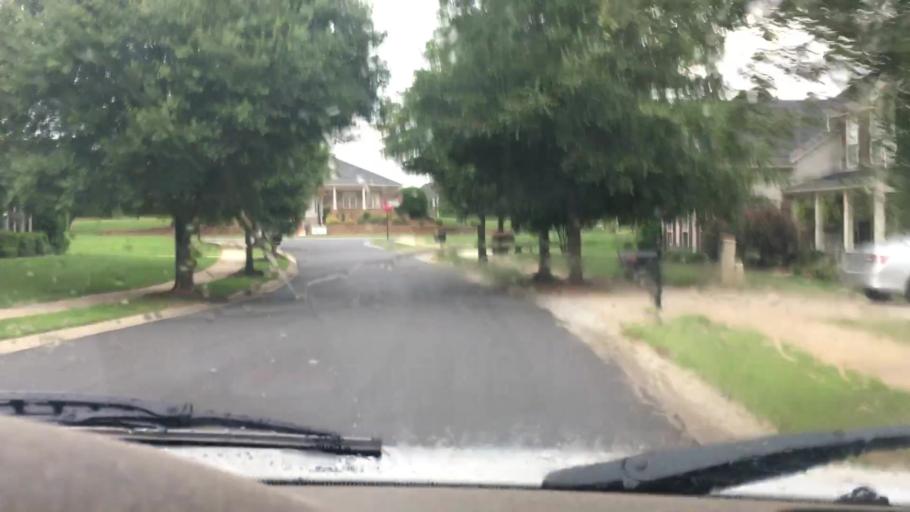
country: US
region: North Carolina
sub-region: Mecklenburg County
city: Huntersville
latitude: 35.4154
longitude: -80.9062
